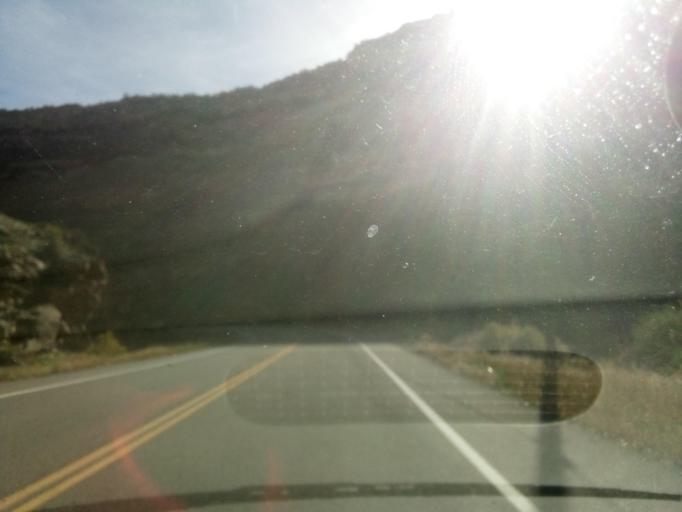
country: US
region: Colorado
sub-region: Mesa County
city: Palisade
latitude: 39.1878
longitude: -108.2626
